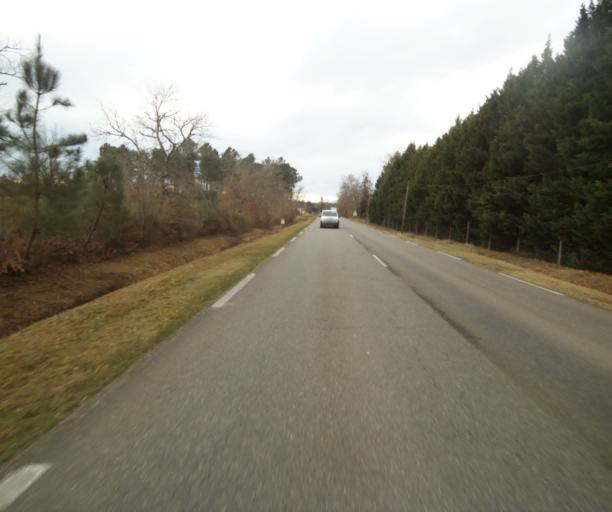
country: FR
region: Aquitaine
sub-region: Departement des Landes
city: Gabarret
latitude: 44.0956
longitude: -0.0187
